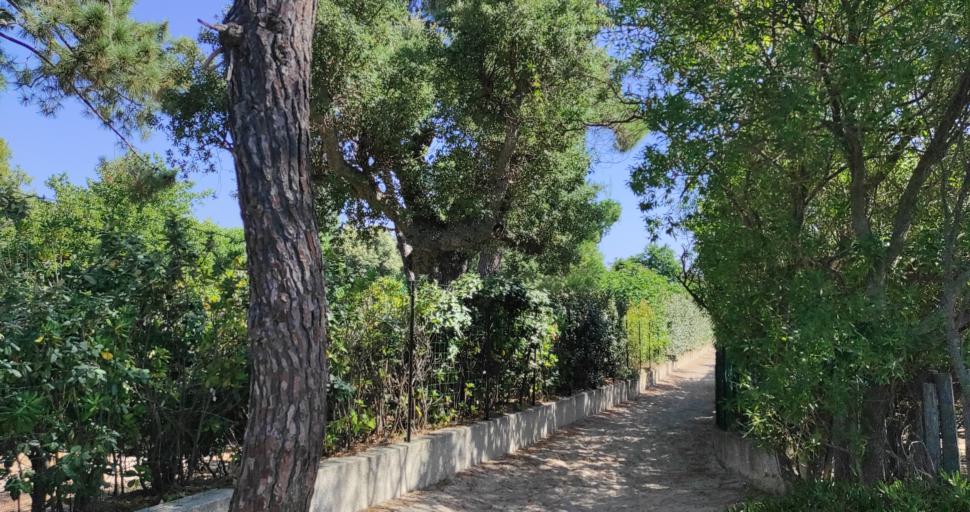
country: FR
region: Corsica
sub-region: Departement de la Corse-du-Sud
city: Porto-Vecchio
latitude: 41.6219
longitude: 9.3357
